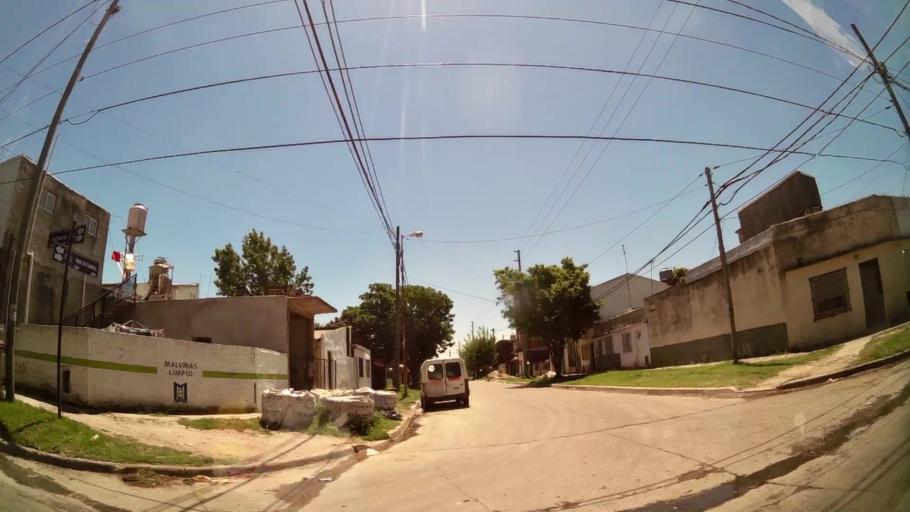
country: AR
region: Buenos Aires
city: Hurlingham
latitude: -34.4915
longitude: -58.6682
